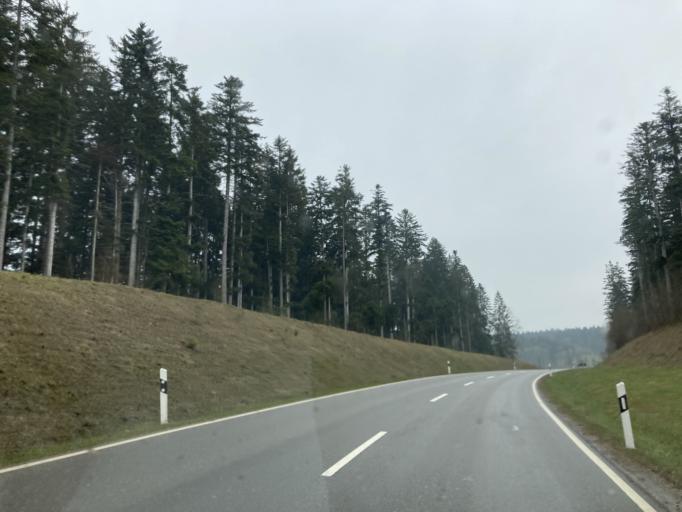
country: DE
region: Baden-Wuerttemberg
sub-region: Karlsruhe Region
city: Lossburg
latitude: 48.3644
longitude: 8.4466
